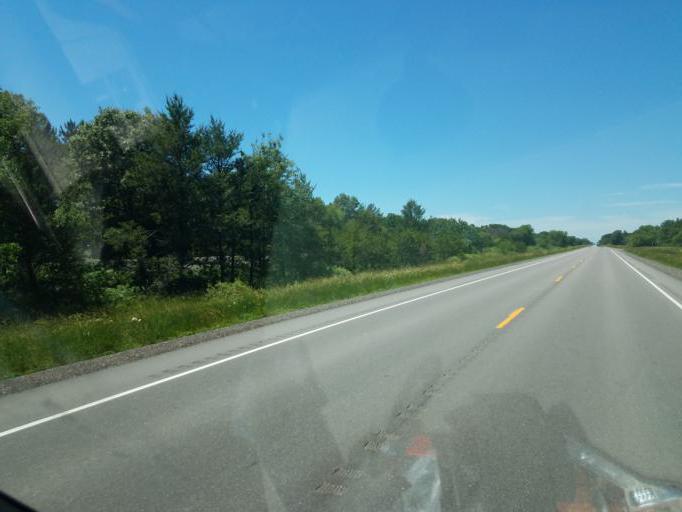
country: US
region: Wisconsin
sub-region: Juneau County
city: New Lisbon
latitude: 44.0249
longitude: -90.1302
